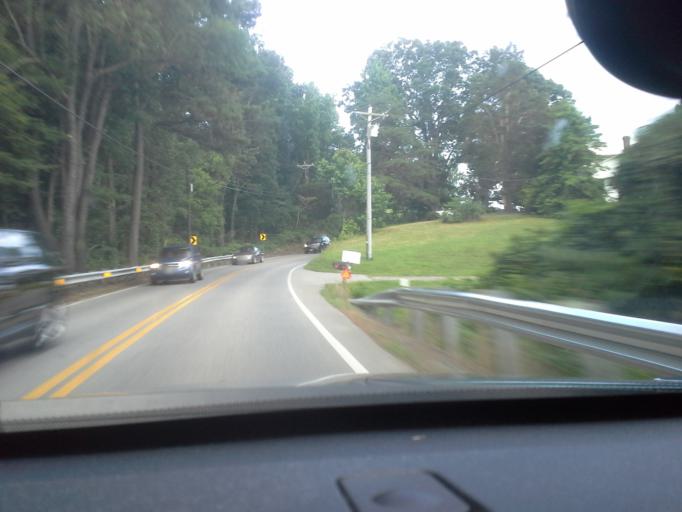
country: US
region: Maryland
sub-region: Calvert County
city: Prince Frederick
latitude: 38.5743
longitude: -76.5362
